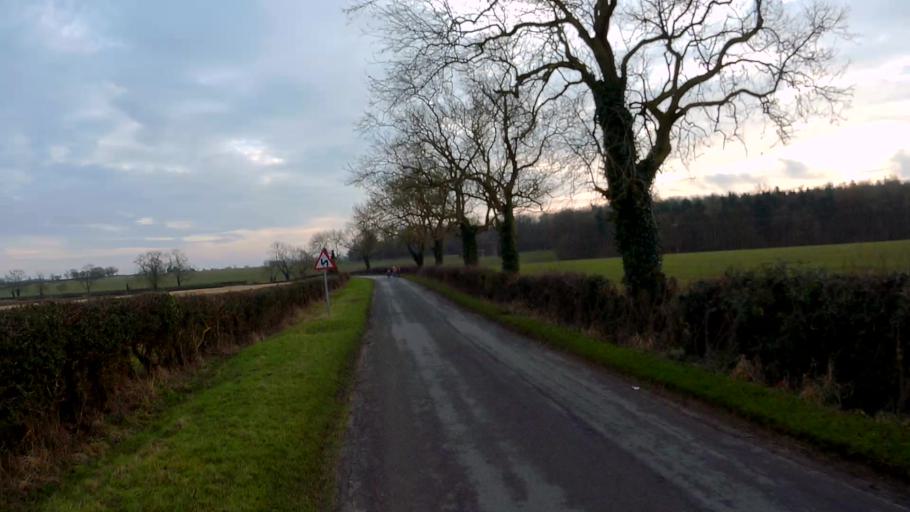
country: GB
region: England
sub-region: Lincolnshire
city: Bourne
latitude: 52.8327
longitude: -0.4471
